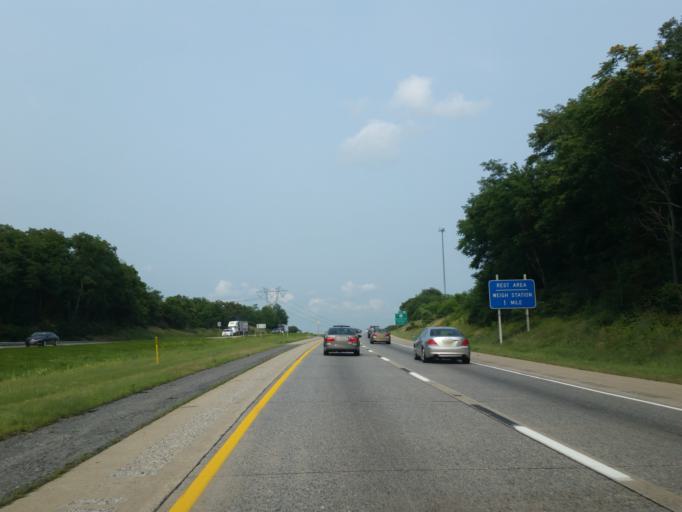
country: US
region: Pennsylvania
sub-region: Dauphin County
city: Skyline View
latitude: 40.3657
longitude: -76.6996
